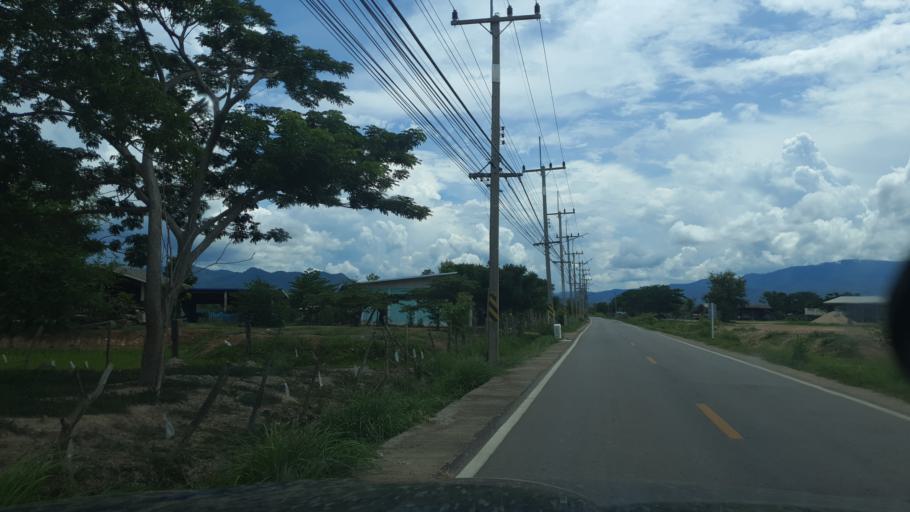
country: TH
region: Lampang
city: Sop Prap
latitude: 17.8811
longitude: 99.3741
